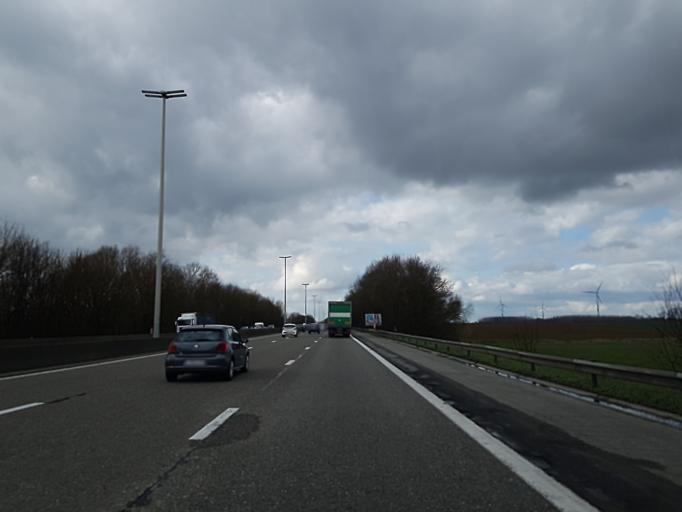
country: BE
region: Wallonia
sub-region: Province du Brabant Wallon
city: Perwez
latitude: 50.5837
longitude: 4.8086
